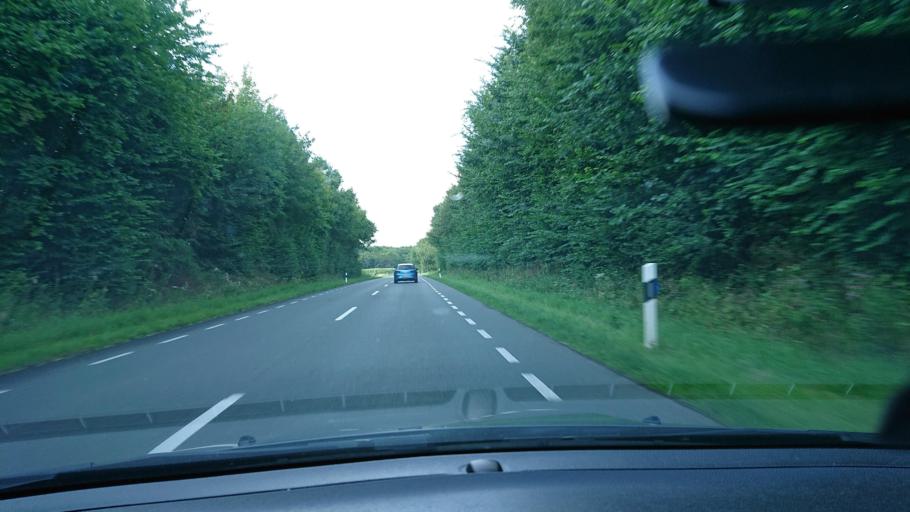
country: DE
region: North Rhine-Westphalia
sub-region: Regierungsbezirk Arnsberg
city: Mohnesee
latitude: 51.4990
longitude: 8.0597
